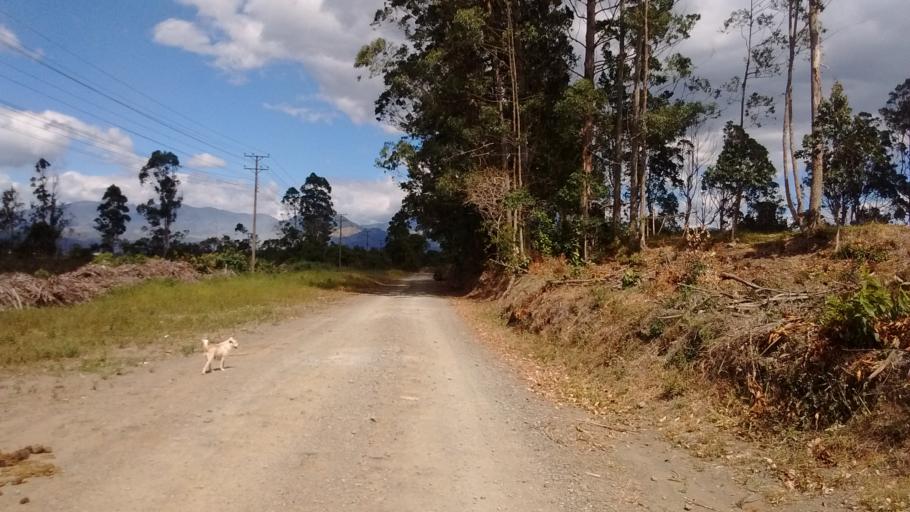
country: CO
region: Cauca
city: Popayan
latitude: 2.4966
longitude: -76.5921
